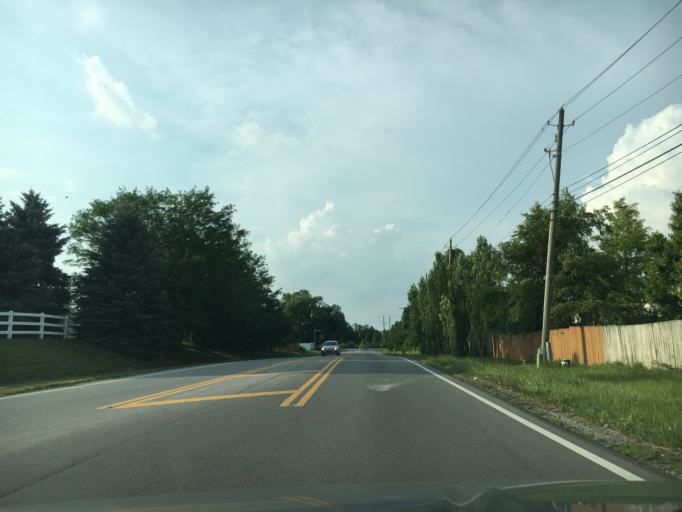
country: US
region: Ohio
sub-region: Franklin County
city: Hilliard
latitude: 40.0020
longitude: -83.1660
